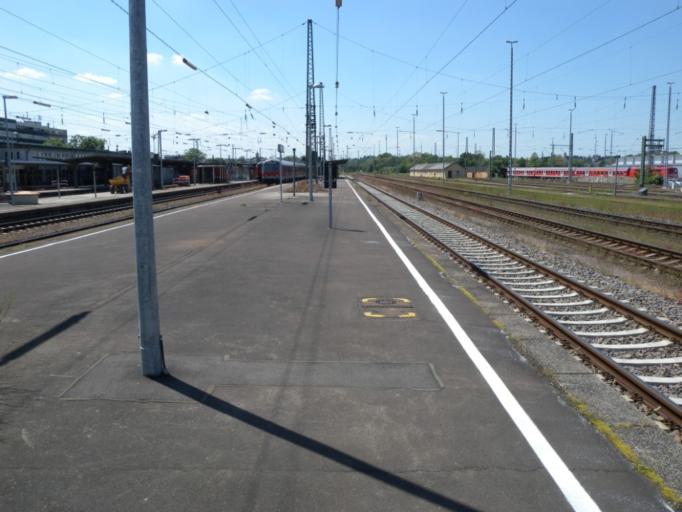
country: DE
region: Baden-Wuerttemberg
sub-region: Regierungsbezirk Stuttgart
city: Heilbronn
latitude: 49.1439
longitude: 9.2093
